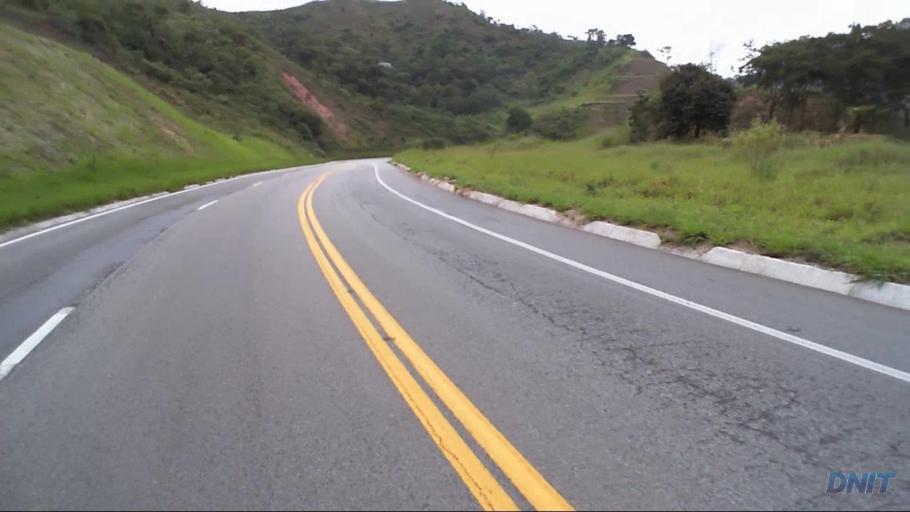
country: BR
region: Minas Gerais
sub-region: Nova Era
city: Nova Era
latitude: -19.6321
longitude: -42.8977
